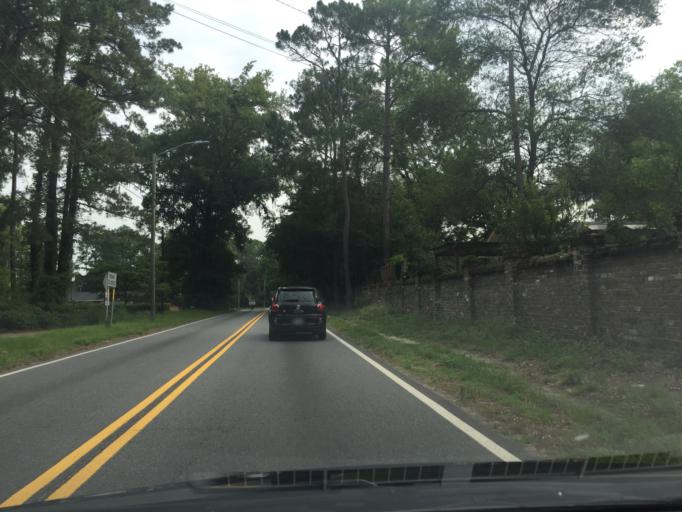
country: US
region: Georgia
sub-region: Chatham County
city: Thunderbolt
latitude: 32.0173
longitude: -81.0974
